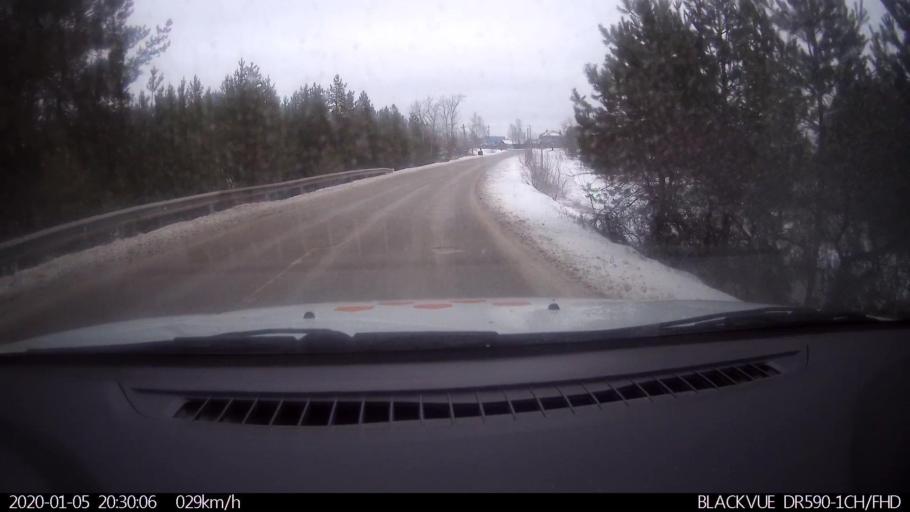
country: RU
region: Nizjnij Novgorod
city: Lukino
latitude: 56.3962
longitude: 43.7292
